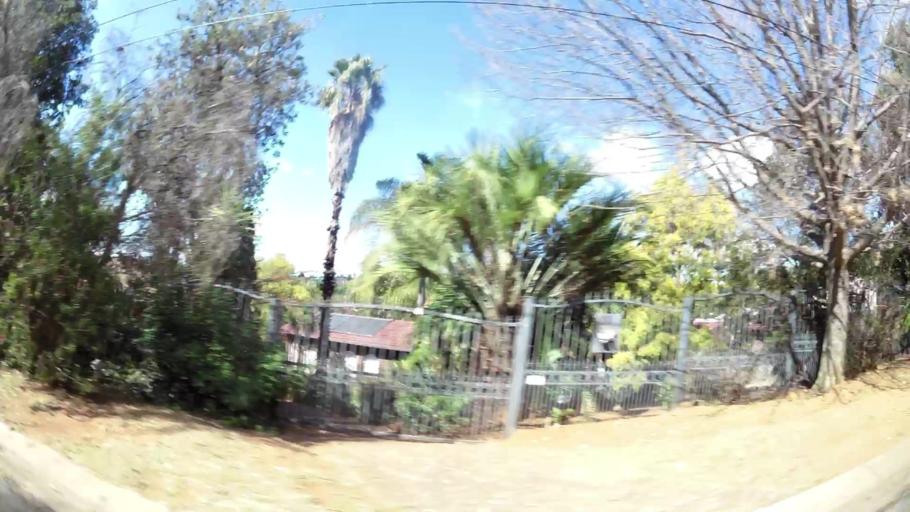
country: ZA
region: Gauteng
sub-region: City of Johannesburg Metropolitan Municipality
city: Roodepoort
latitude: -26.1164
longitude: 27.8425
